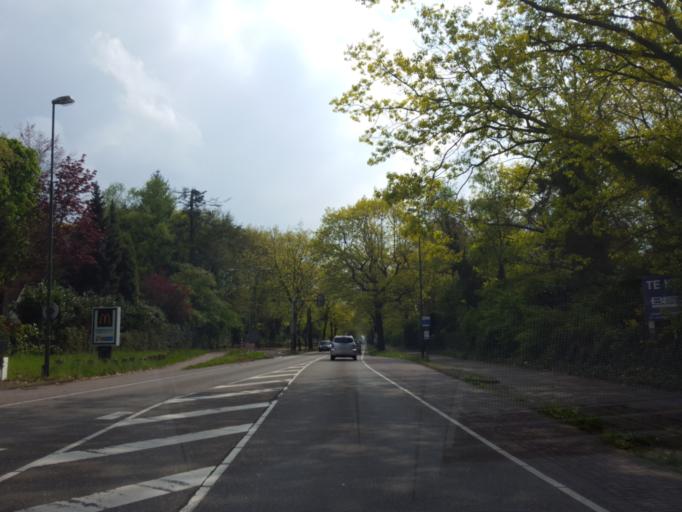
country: NL
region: North Brabant
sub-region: Gemeente Waalre
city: Waalre
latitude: 51.3923
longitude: 5.4749
